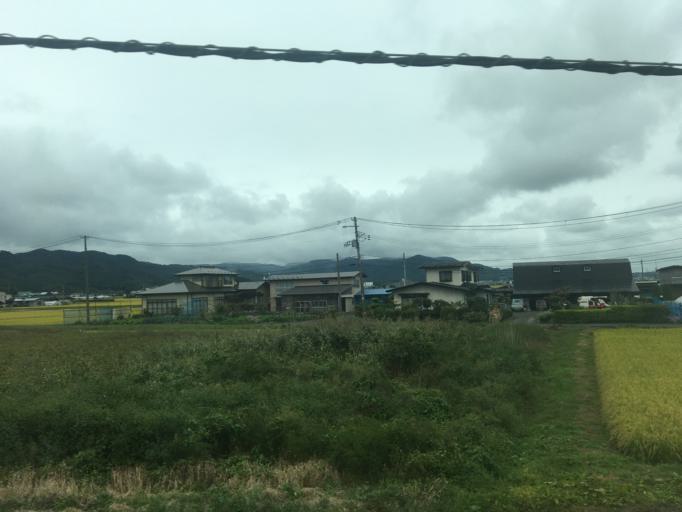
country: JP
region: Iwate
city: Morioka-shi
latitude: 39.7151
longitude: 141.0821
